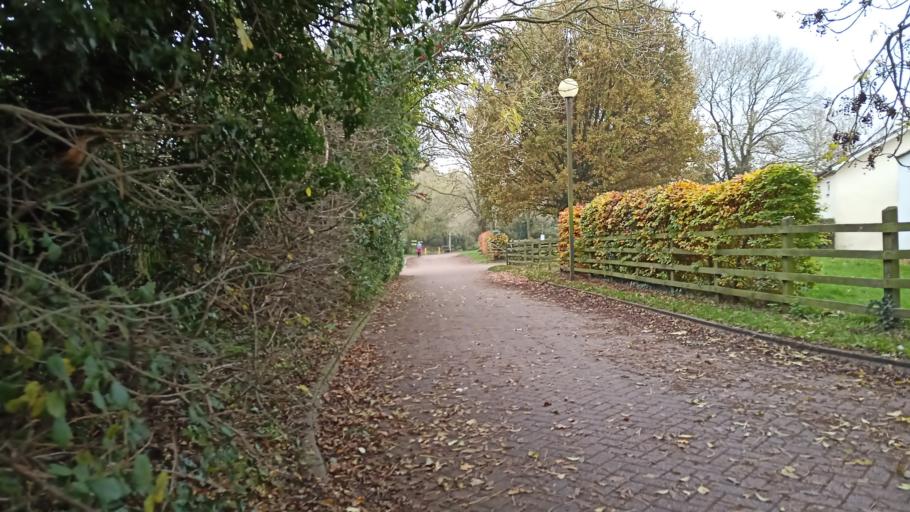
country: GB
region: England
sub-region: Milton Keynes
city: Shenley Church End
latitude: 52.0130
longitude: -0.7834
